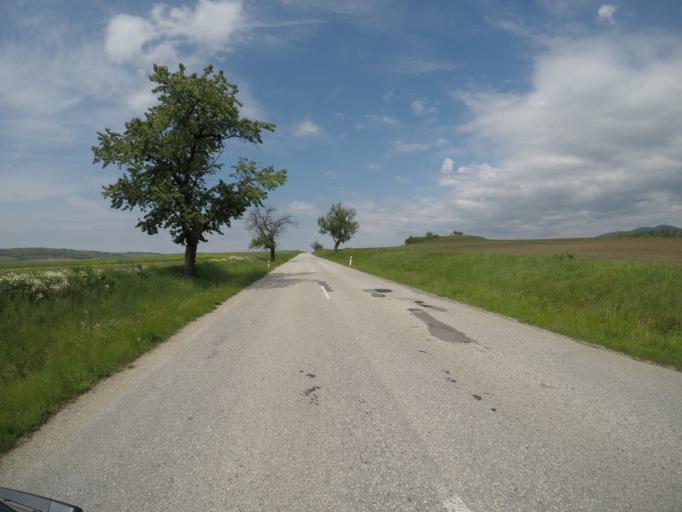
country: HU
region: Komarom-Esztergom
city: Esztergom
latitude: 47.9050
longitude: 18.7549
